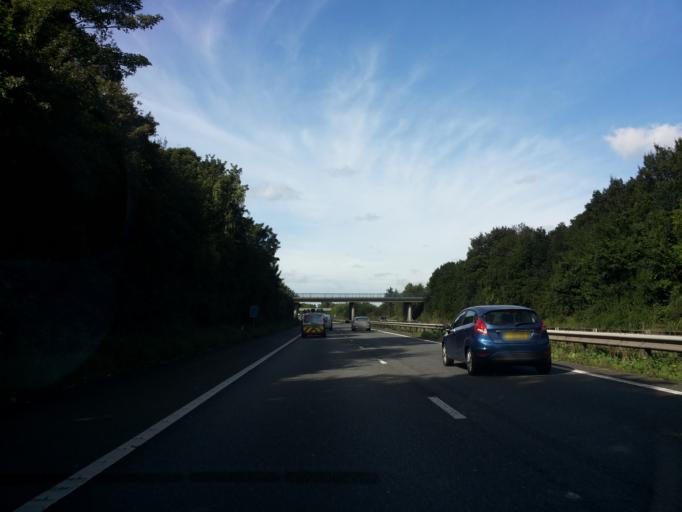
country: GB
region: England
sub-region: Kent
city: Sittingbourne
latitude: 51.3156
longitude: 0.7005
